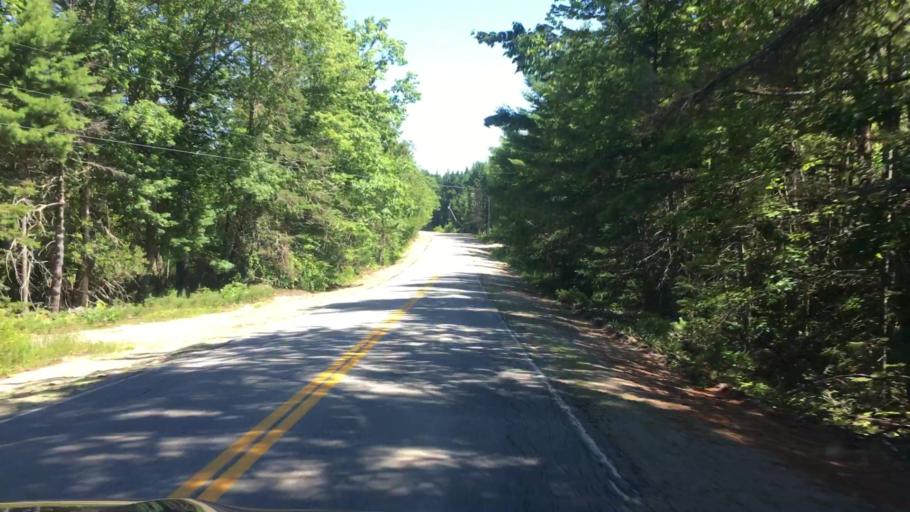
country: US
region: Maine
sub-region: Hancock County
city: Penobscot
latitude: 44.4439
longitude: -68.7038
